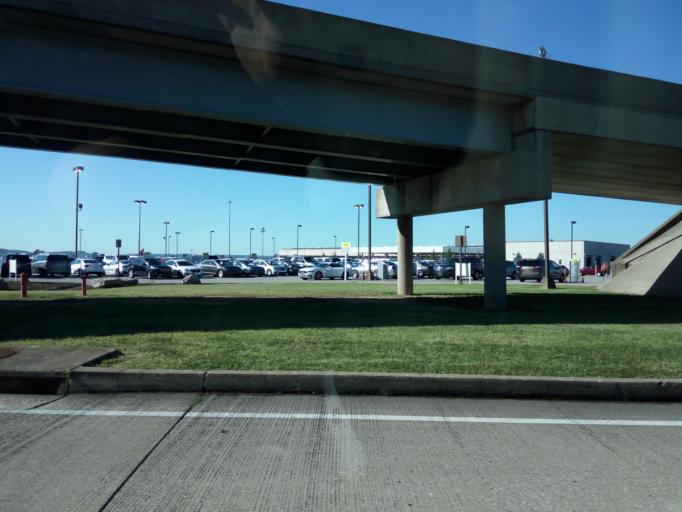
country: US
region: Kentucky
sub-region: Jefferson County
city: Audubon Park
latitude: 38.1861
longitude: -85.7435
